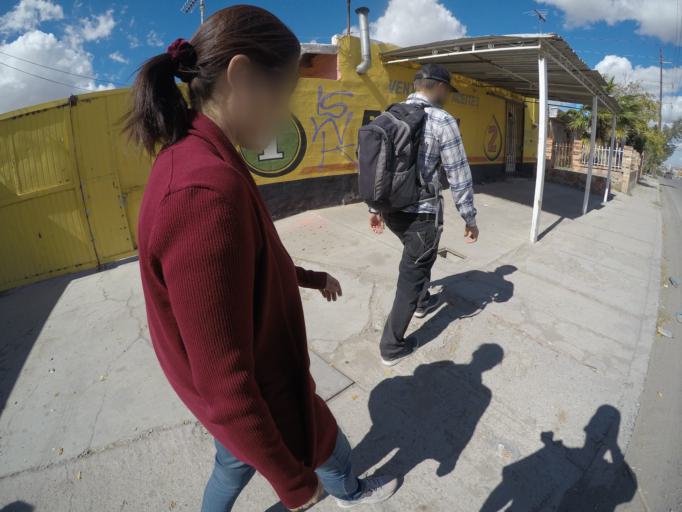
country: MX
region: Chihuahua
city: Ciudad Juarez
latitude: 31.6927
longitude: -106.4812
